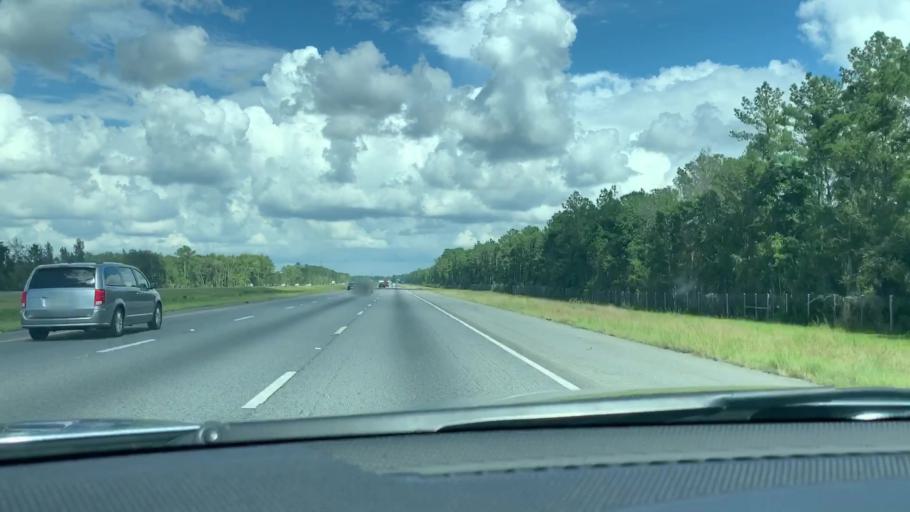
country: US
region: Georgia
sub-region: Glynn County
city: Brunswick
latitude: 31.0748
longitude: -81.6205
